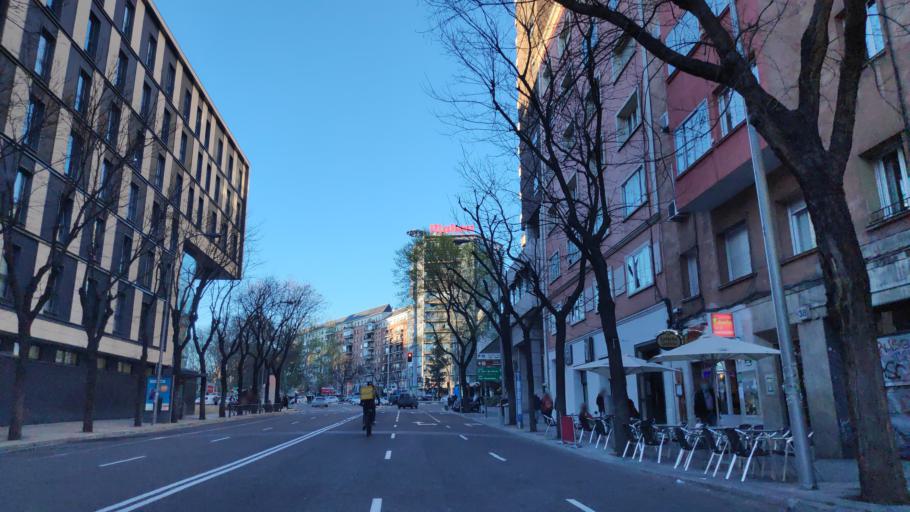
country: ES
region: Madrid
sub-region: Provincia de Madrid
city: Moncloa-Aravaca
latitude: 40.4382
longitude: -3.7178
